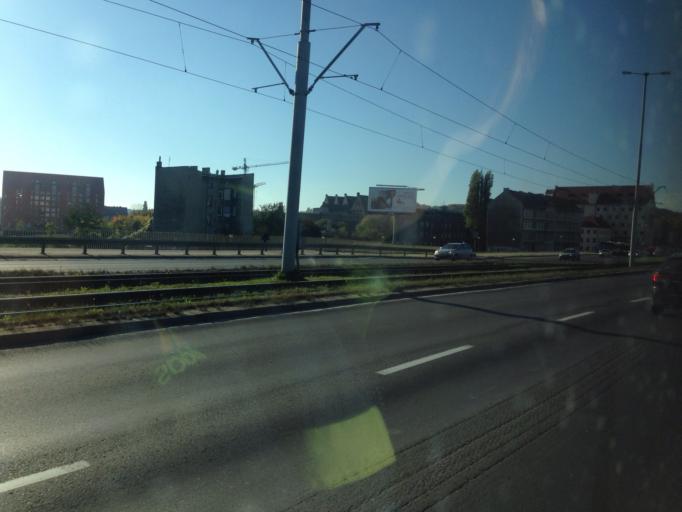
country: PL
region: Pomeranian Voivodeship
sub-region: Gdansk
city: Gdansk
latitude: 54.3451
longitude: 18.6597
